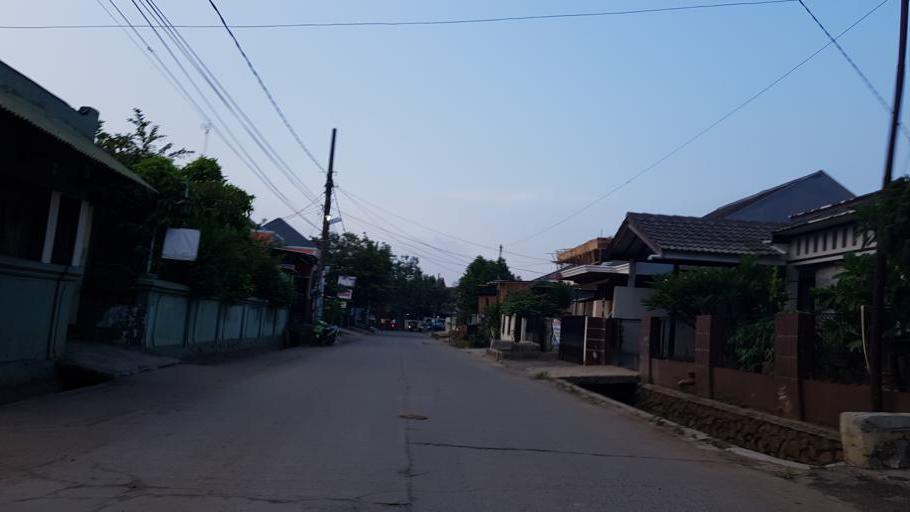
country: ID
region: West Java
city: Bekasi
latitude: -6.2715
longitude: 106.9469
